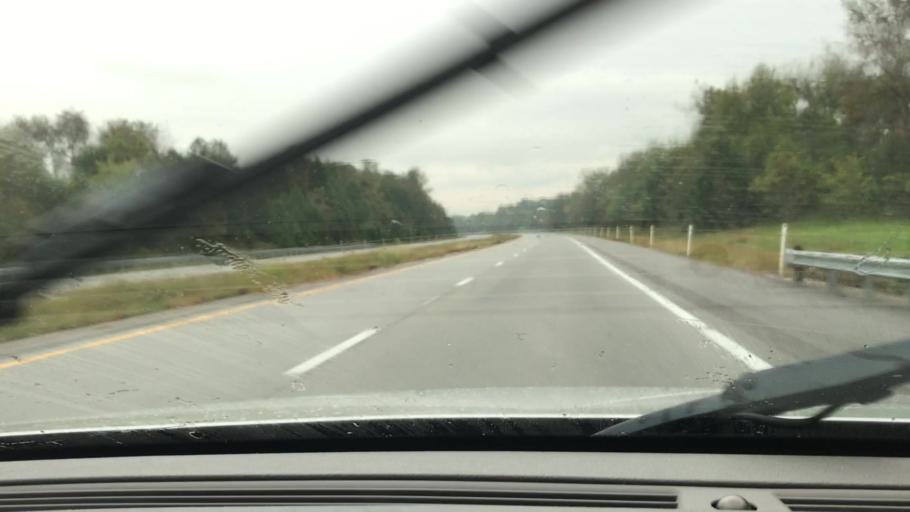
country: US
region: Kentucky
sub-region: Barren County
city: Glasgow
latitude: 37.0173
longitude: -86.0319
